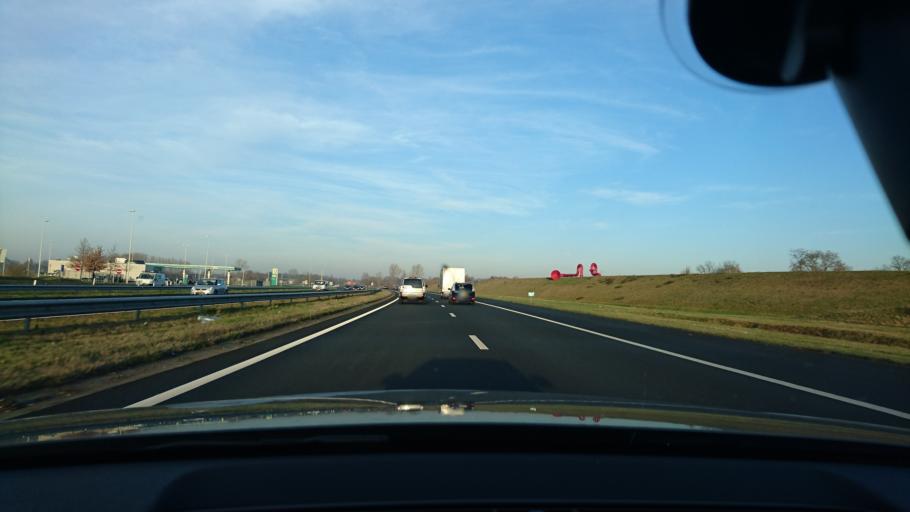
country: NL
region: North Brabant
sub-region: Gemeente Son en Breugel
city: Son
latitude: 51.5342
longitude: 5.4790
